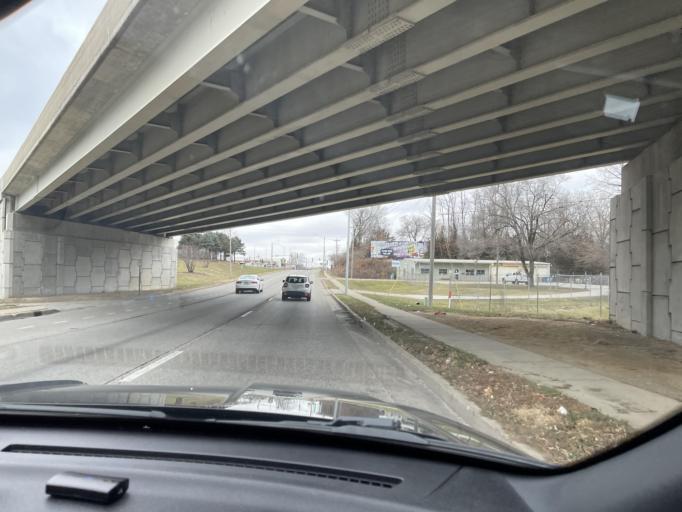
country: US
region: Illinois
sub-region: Sangamon County
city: Leland Grove
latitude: 39.8062
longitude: -89.6749
